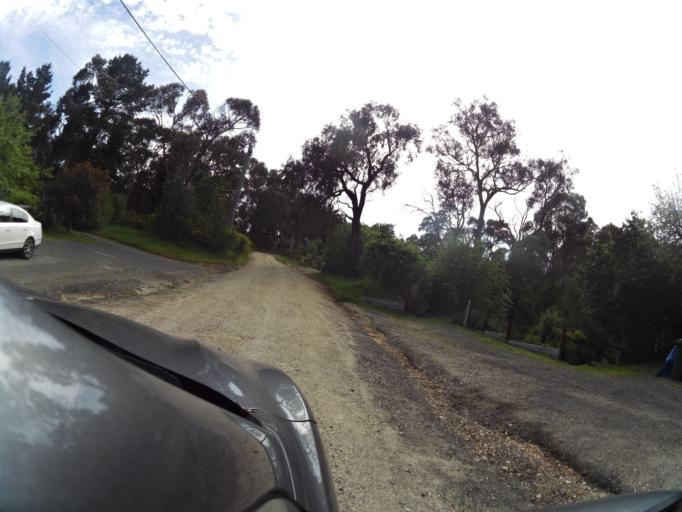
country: AU
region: Victoria
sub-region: Mount Alexander
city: Castlemaine
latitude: -37.3070
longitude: 144.1420
